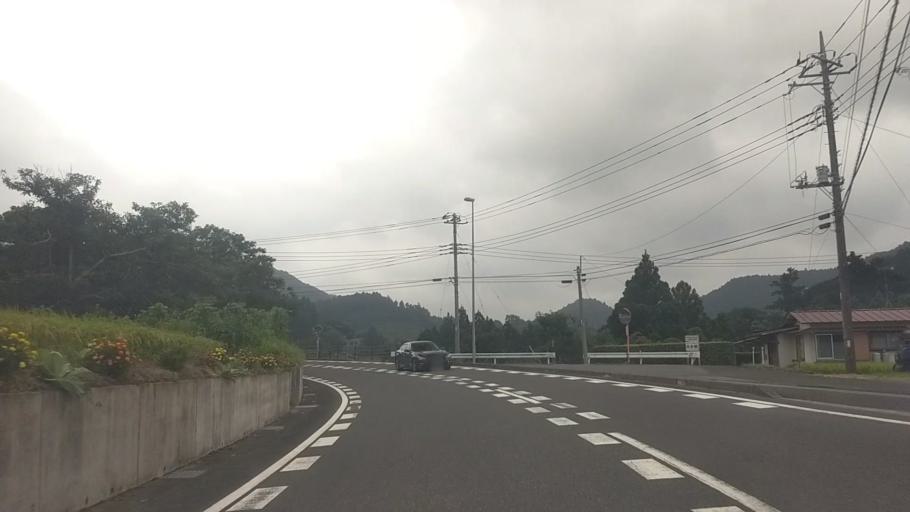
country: JP
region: Chiba
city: Kawaguchi
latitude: 35.2206
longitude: 140.1344
